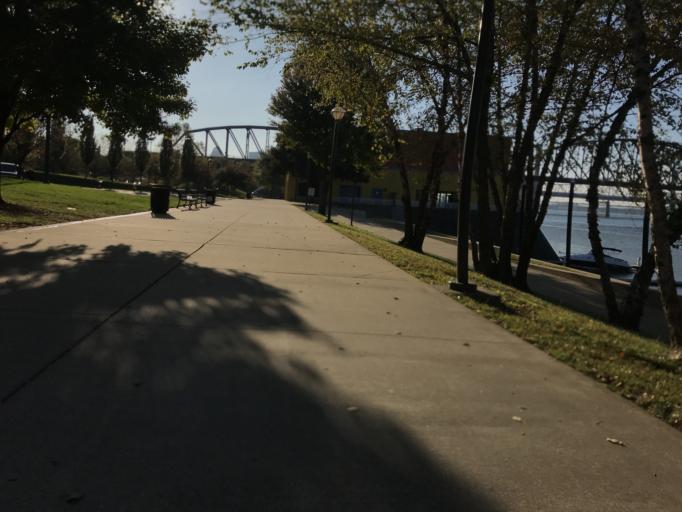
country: US
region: Indiana
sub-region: Clark County
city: Jeffersonville
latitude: 38.2635
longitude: -85.7339
